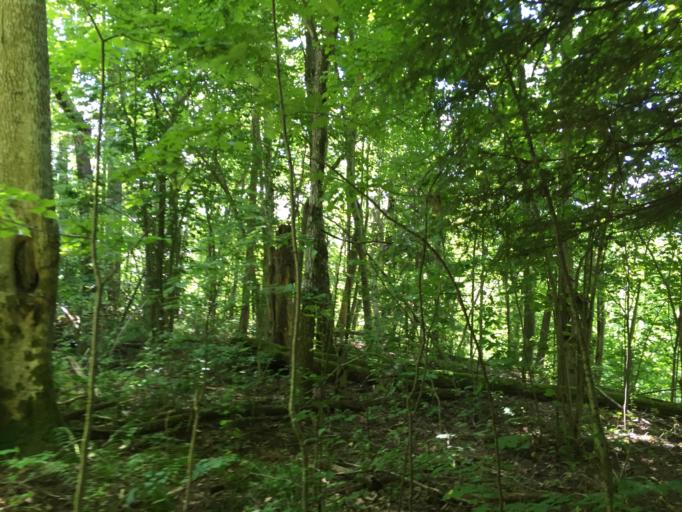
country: LV
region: Sigulda
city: Sigulda
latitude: 57.1879
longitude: 24.9331
